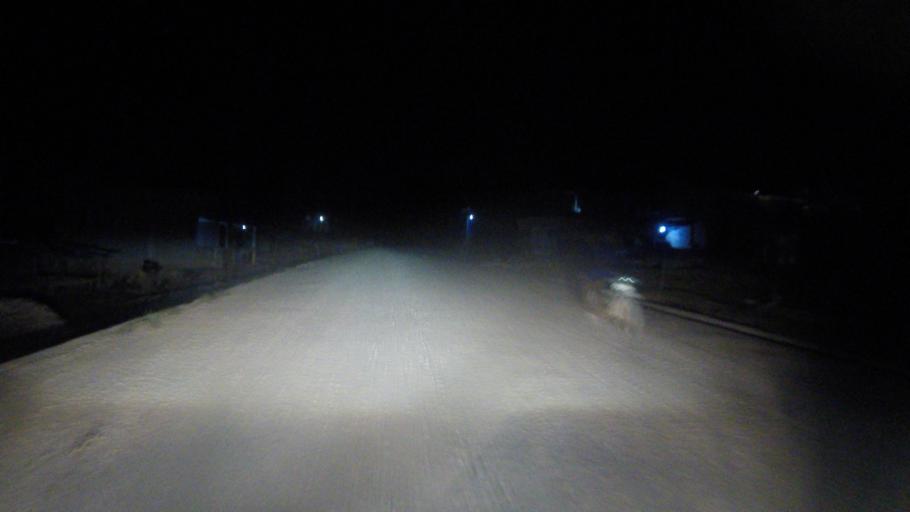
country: TL
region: Viqueque
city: Viqueque
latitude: -8.8356
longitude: 126.5190
